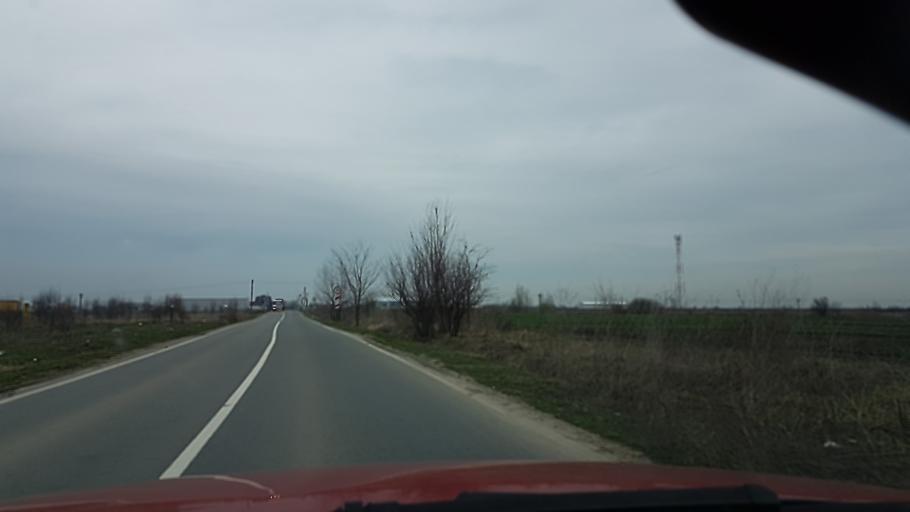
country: RO
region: Ilfov
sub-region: Comuna Balotesti
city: Balotesti
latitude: 44.6001
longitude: 26.1322
